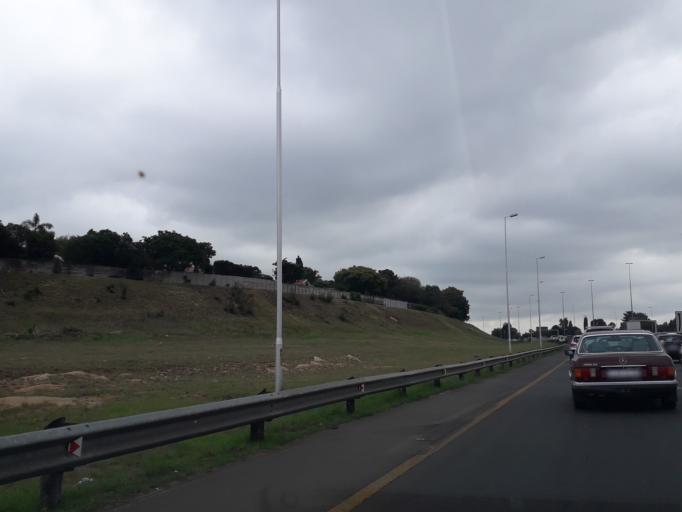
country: ZA
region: Gauteng
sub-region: City of Johannesburg Metropolitan Municipality
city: Roodepoort
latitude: -26.1134
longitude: 27.9550
